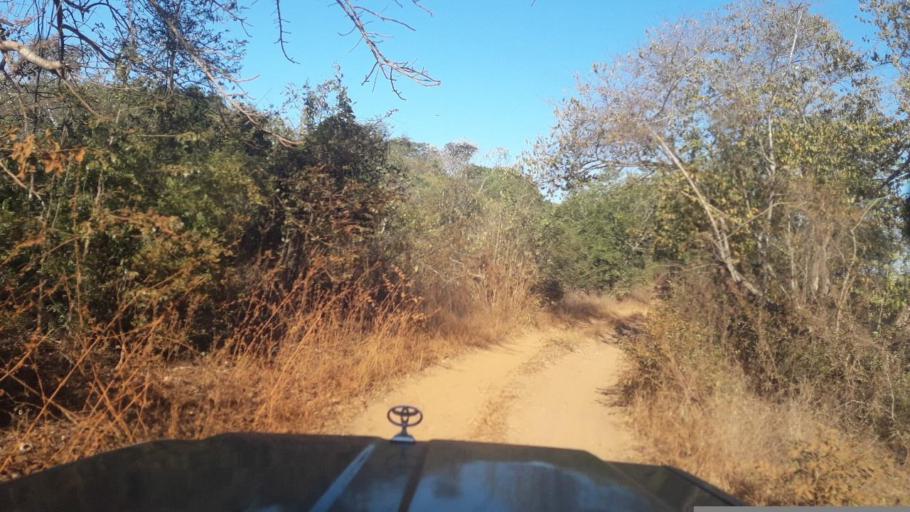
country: MG
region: Boeny
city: Sitampiky
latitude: -16.4261
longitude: 45.6227
